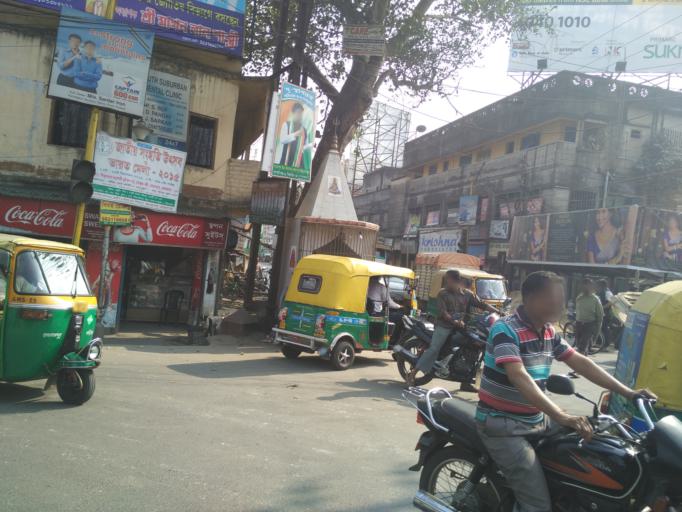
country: IN
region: West Bengal
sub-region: South 24 Paraganas
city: Baruipur
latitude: 22.4474
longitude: 88.3919
